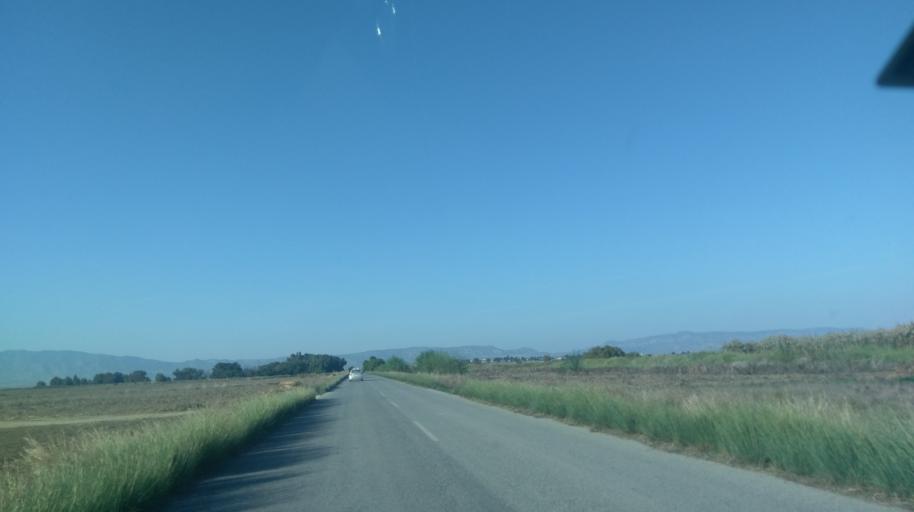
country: CY
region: Ammochostos
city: Lefkonoiko
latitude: 35.1959
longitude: 33.6959
